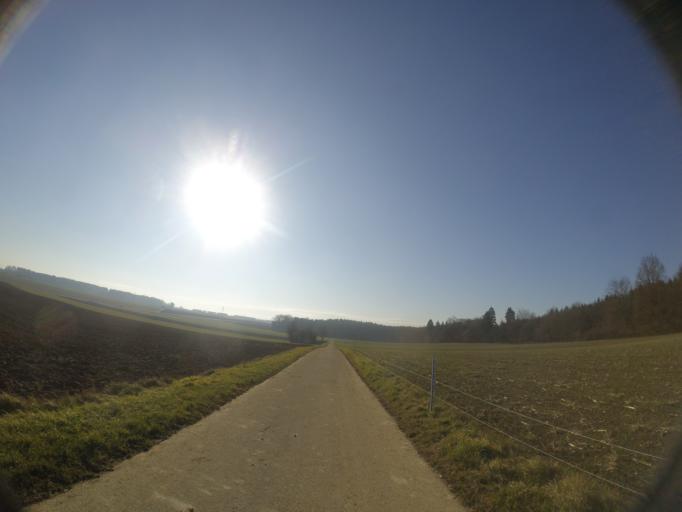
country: DE
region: Baden-Wuerttemberg
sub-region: Tuebingen Region
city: Beimerstetten
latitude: 48.4799
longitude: 9.9697
